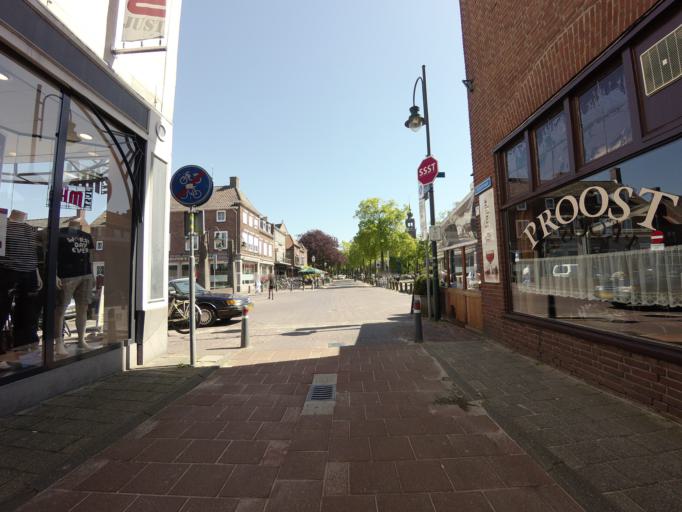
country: NL
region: North Brabant
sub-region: Gemeente Moerdijk
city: Klundert
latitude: 51.6456
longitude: 4.6057
